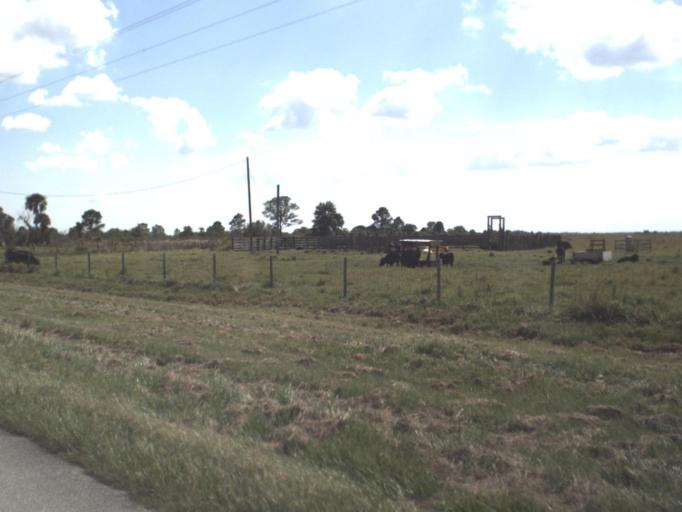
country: US
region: Florida
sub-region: Okeechobee County
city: Okeechobee
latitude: 27.3702
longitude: -80.9769
